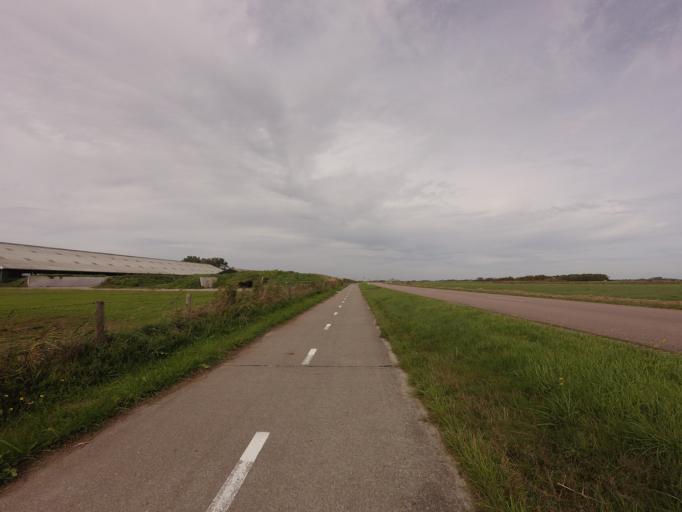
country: NL
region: North Holland
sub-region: Gemeente Texel
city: Den Burg
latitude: 53.0489
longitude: 4.8484
